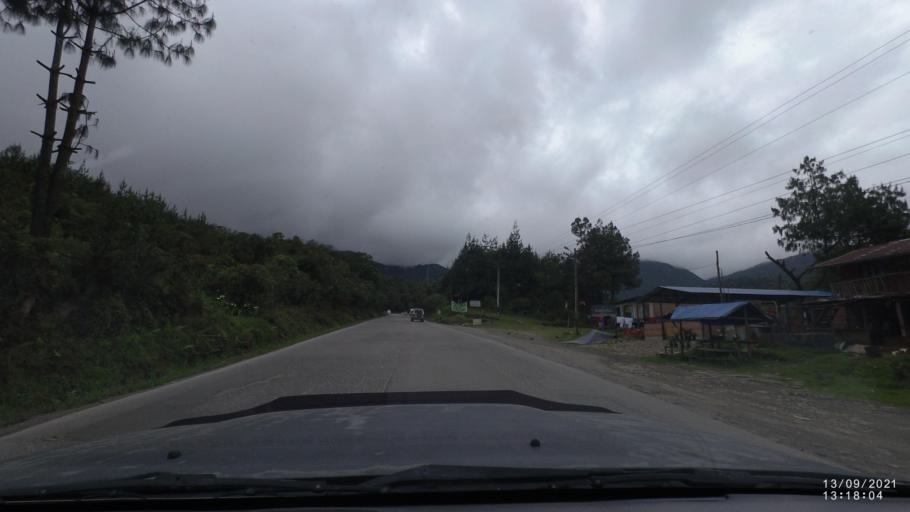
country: BO
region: Cochabamba
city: Colomi
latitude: -17.2004
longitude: -65.8643
